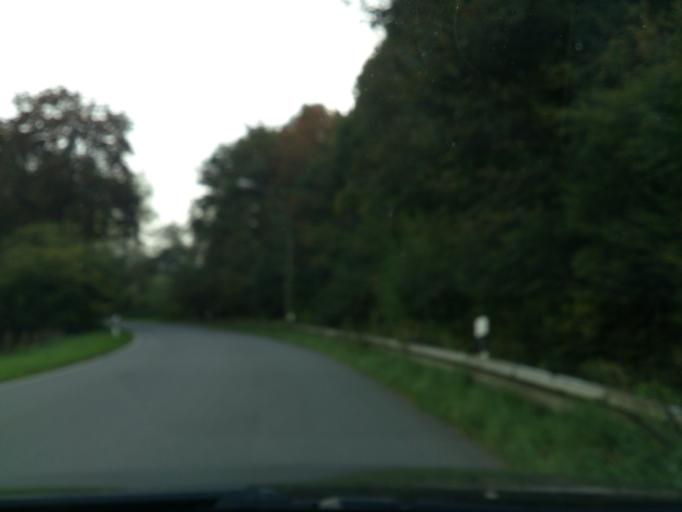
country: DE
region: North Rhine-Westphalia
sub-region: Regierungsbezirk Detmold
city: Willebadessen
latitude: 51.5354
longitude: 9.0314
